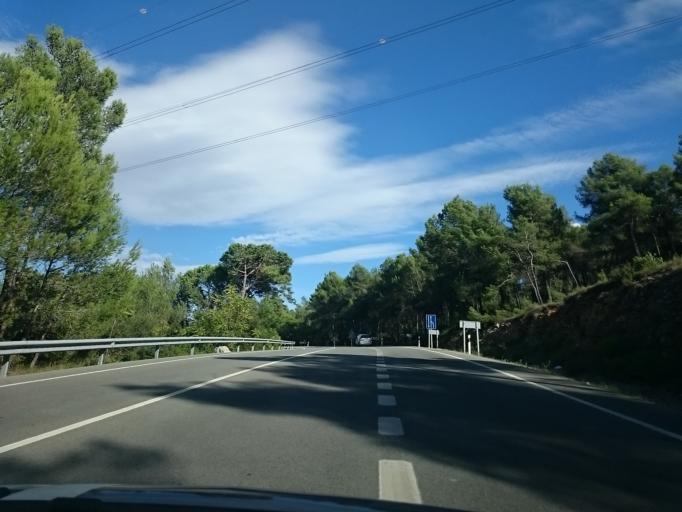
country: ES
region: Catalonia
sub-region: Provincia de Barcelona
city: Subirats
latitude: 41.3907
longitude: 1.8265
